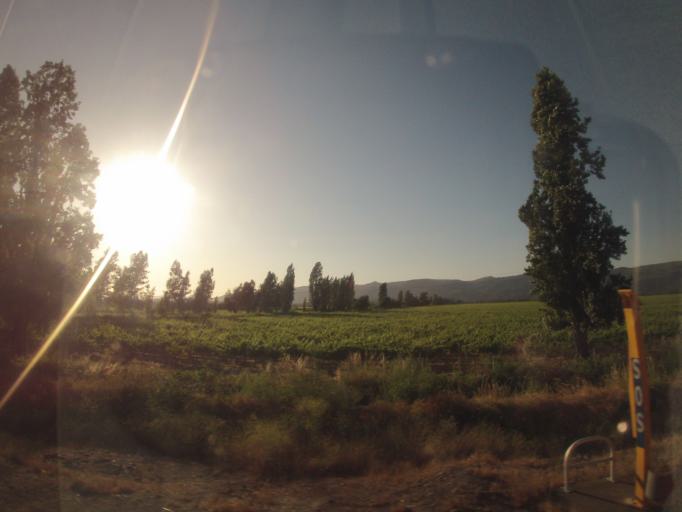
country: CL
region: O'Higgins
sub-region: Provincia de Colchagua
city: Chimbarongo
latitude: -34.7400
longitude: -71.0411
